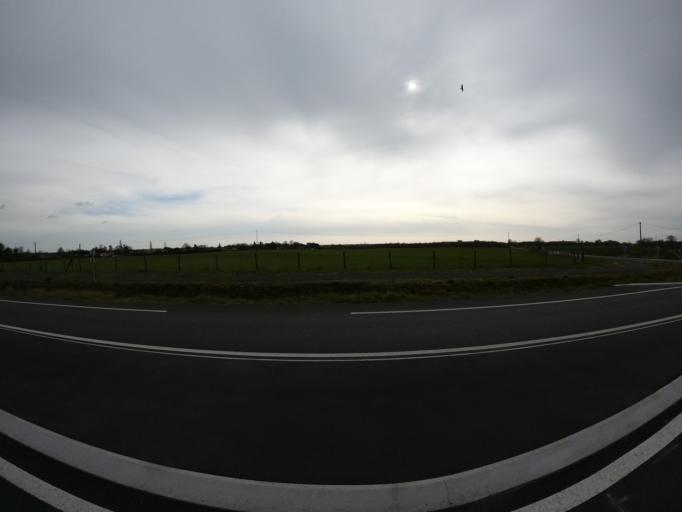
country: FR
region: Pays de la Loire
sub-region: Departement de la Vendee
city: Montaigu
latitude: 46.9833
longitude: -1.2933
